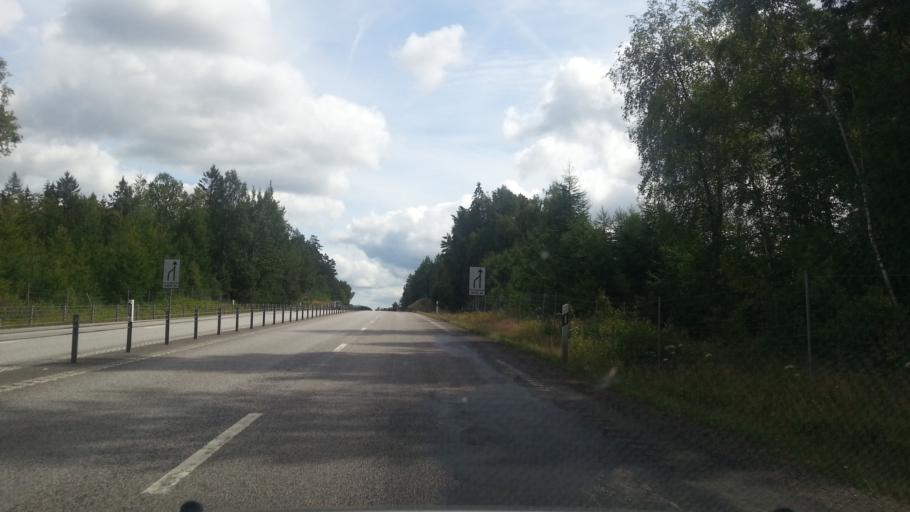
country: SE
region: Vaestra Goetaland
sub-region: Gullspangs Kommun
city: Hova
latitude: 58.8070
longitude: 14.1112
